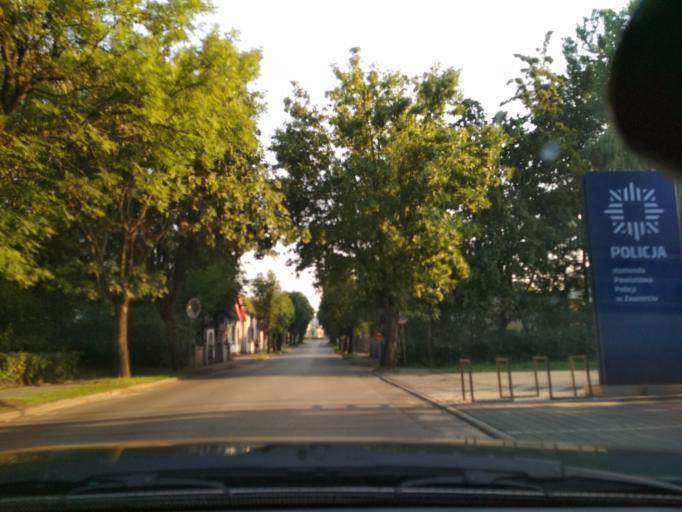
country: PL
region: Silesian Voivodeship
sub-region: Powiat zawiercianski
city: Zawiercie
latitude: 50.4843
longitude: 19.4349
